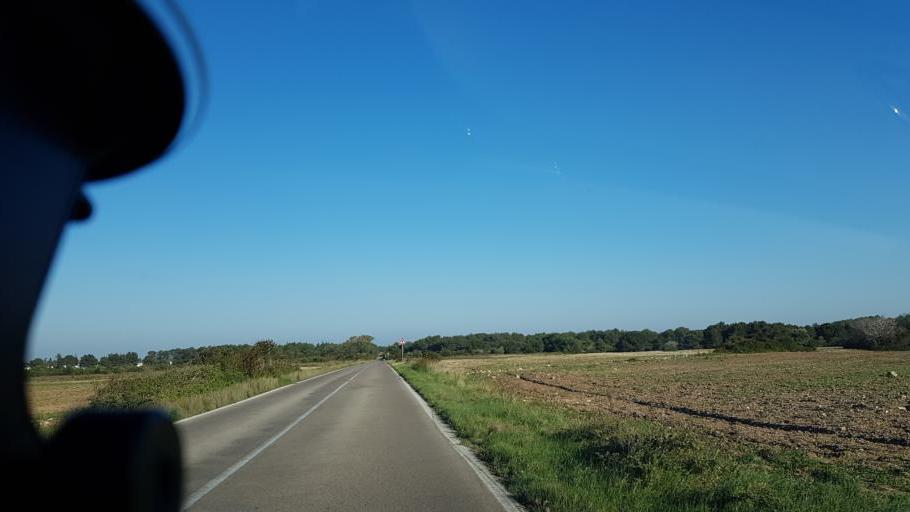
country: IT
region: Apulia
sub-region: Provincia di Lecce
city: Struda
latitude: 40.3915
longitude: 18.2847
